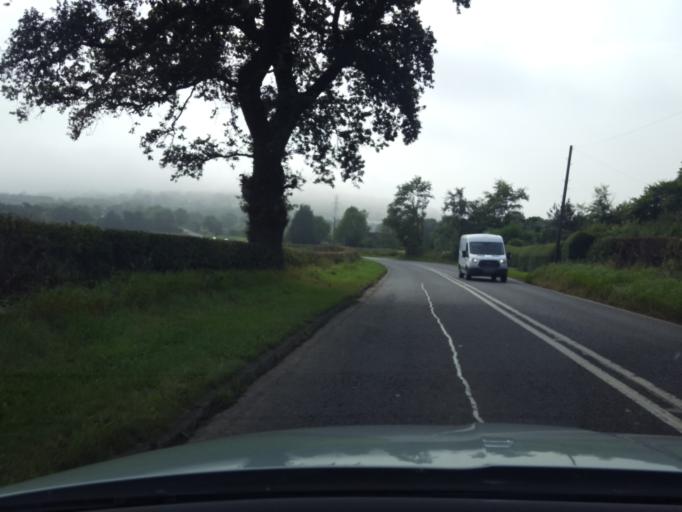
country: GB
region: Scotland
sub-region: Fife
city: Inverkeithing
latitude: 56.0453
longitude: -3.3903
